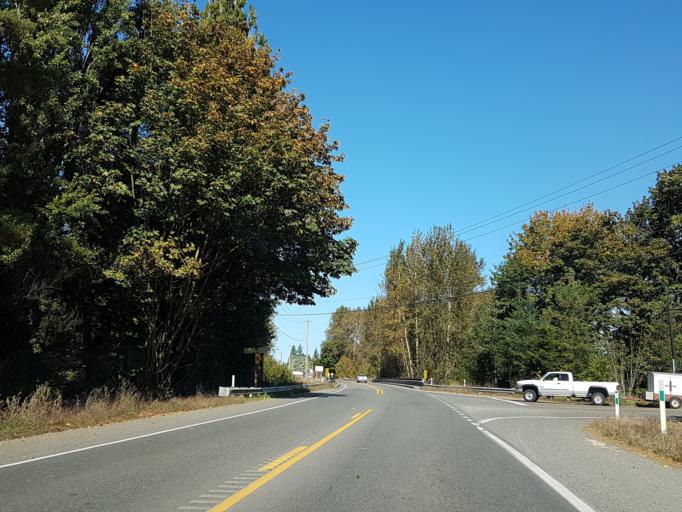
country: US
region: Washington
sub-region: Snohomish County
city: Monroe
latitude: 47.8424
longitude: -121.9693
